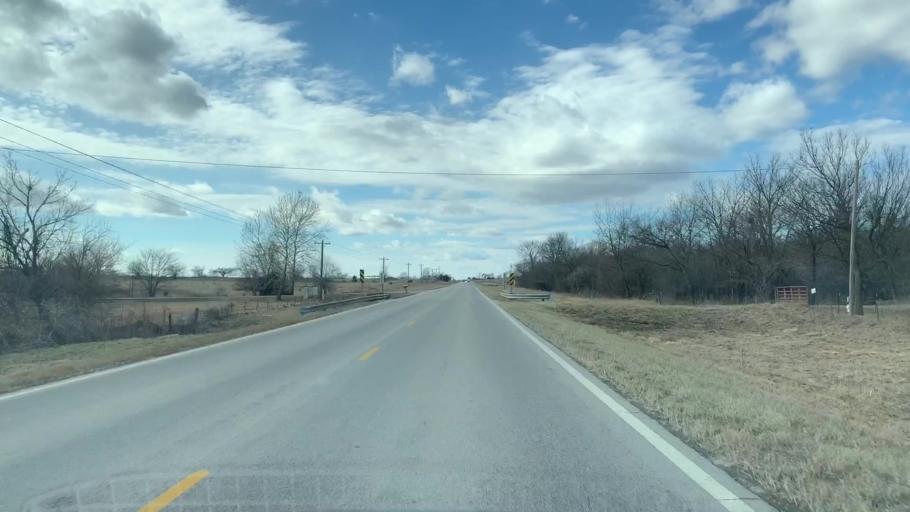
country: US
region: Kansas
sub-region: Neosho County
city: Erie
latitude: 37.5294
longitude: -95.2938
